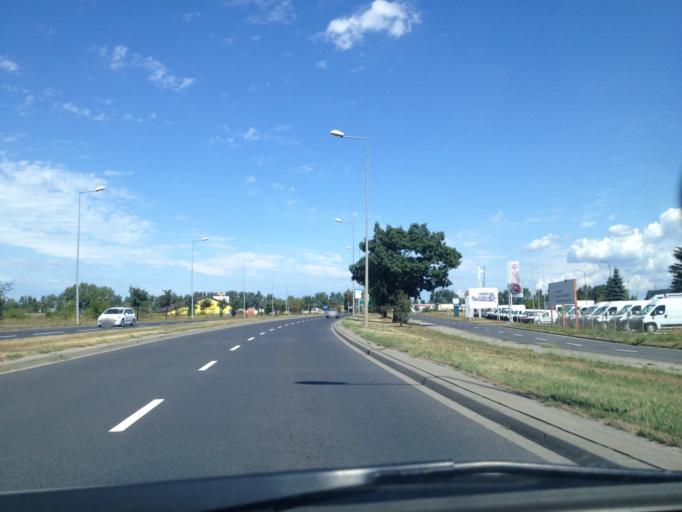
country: PL
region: Lower Silesian Voivodeship
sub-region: Legnica
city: Legnica
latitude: 51.1721
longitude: 16.1717
